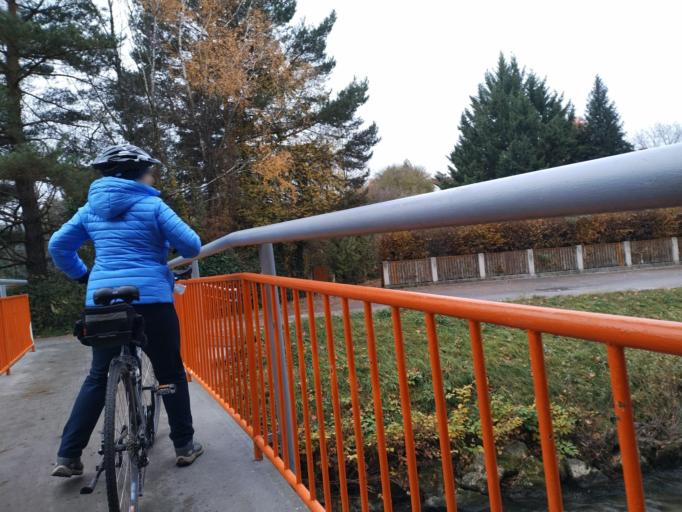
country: AT
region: Lower Austria
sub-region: Politischer Bezirk Neunkirchen
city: Pitten
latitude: 47.7133
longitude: 16.1814
